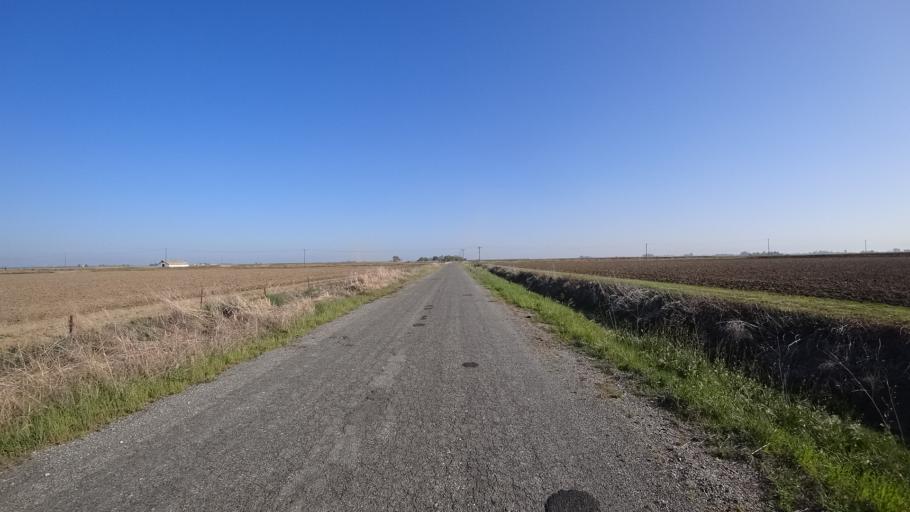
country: US
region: California
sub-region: Glenn County
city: Willows
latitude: 39.5515
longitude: -122.1321
